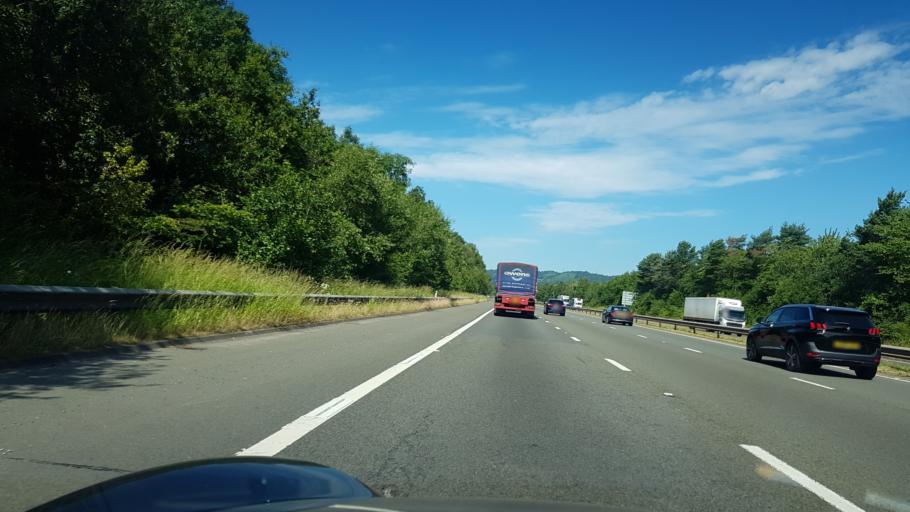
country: GB
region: Wales
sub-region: Caerphilly County Borough
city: Machen
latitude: 51.5448
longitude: -3.1477
